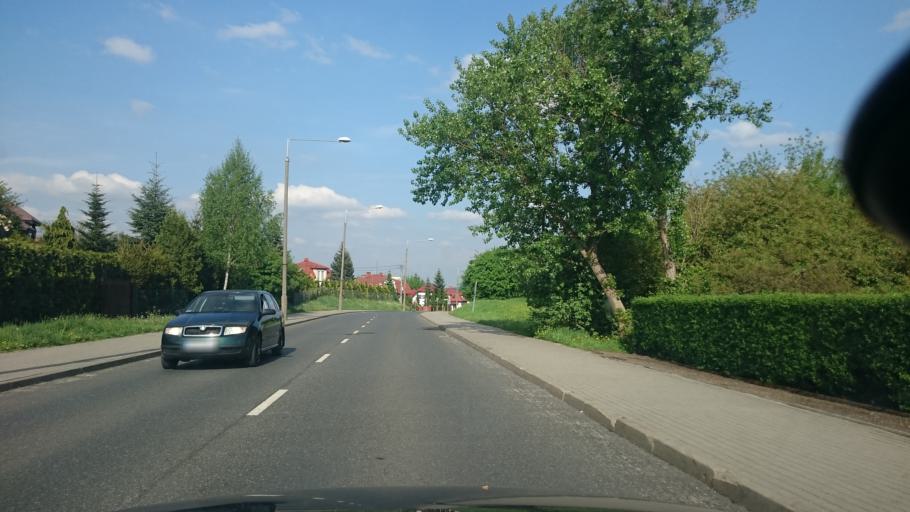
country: PL
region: Kujawsko-Pomorskie
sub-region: Grudziadz
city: Grudziadz
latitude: 53.4601
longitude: 18.7352
